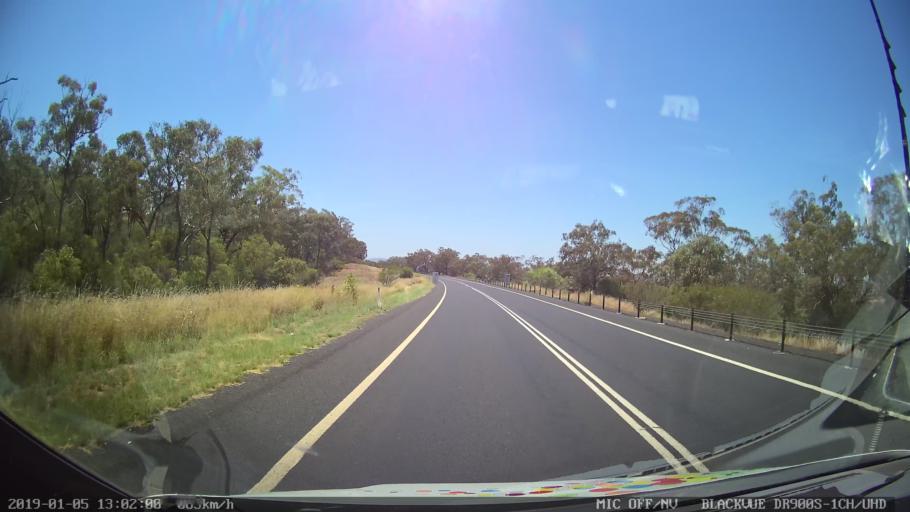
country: AU
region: New South Wales
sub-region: Narrabri
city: Boggabri
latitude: -31.1166
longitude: 149.8052
